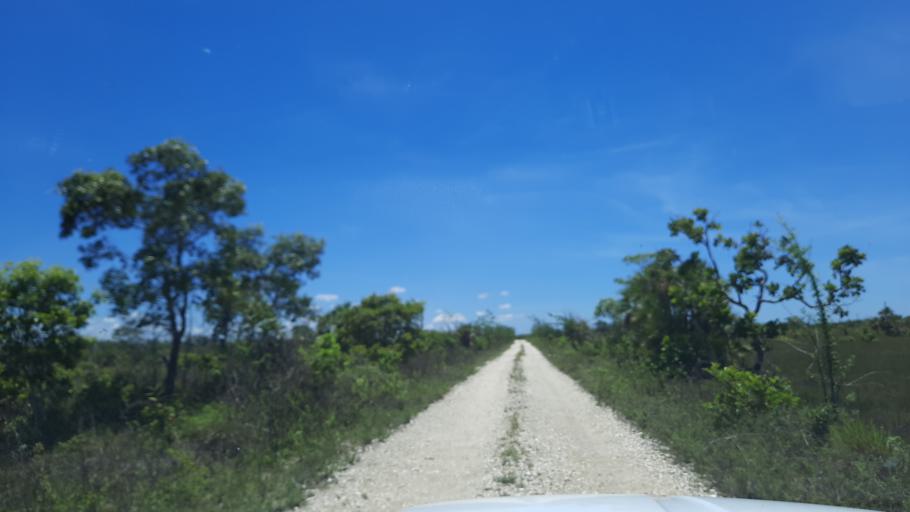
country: BZ
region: Cayo
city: Belmopan
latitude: 17.3822
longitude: -88.4964
